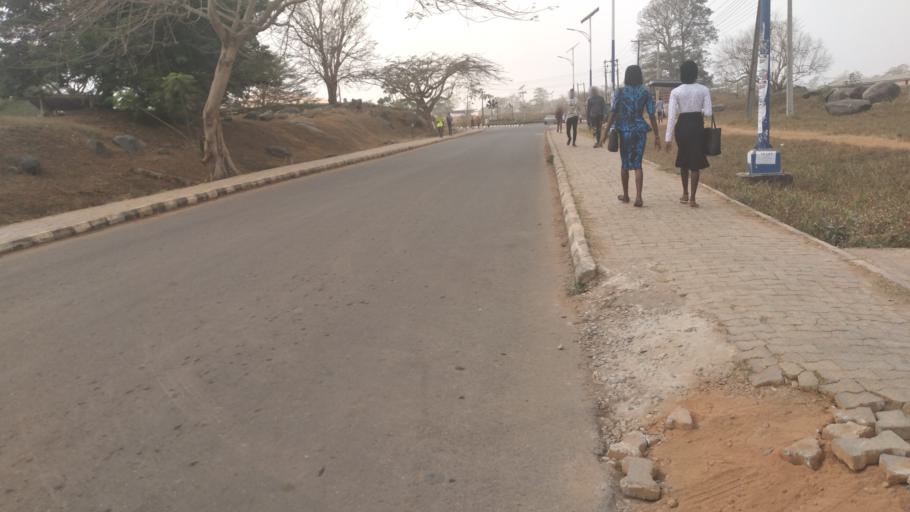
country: NG
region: Ondo
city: Ilare
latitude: 7.3026
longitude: 5.1397
